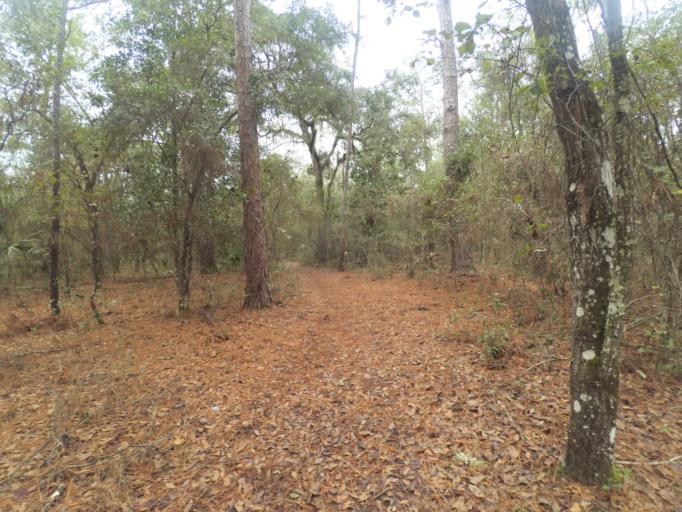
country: US
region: Florida
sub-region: Alachua County
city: Gainesville
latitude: 29.5458
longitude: -82.2734
